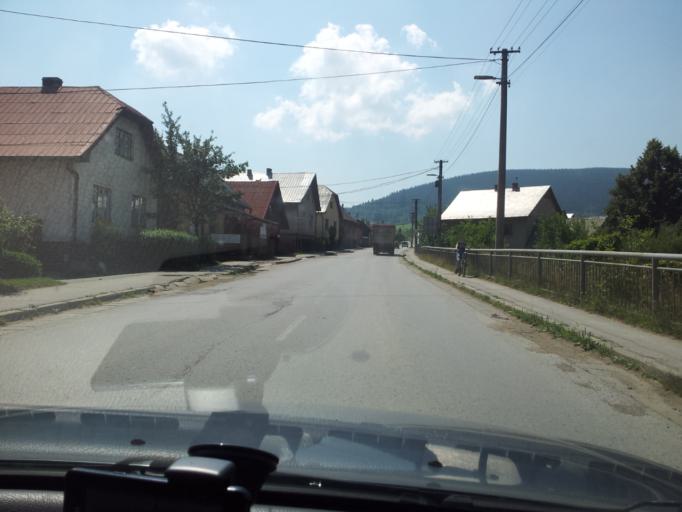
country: SK
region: Zilinsky
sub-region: Okres Dolny Kubin
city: Dolny Kubin
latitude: 49.3230
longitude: 19.3486
